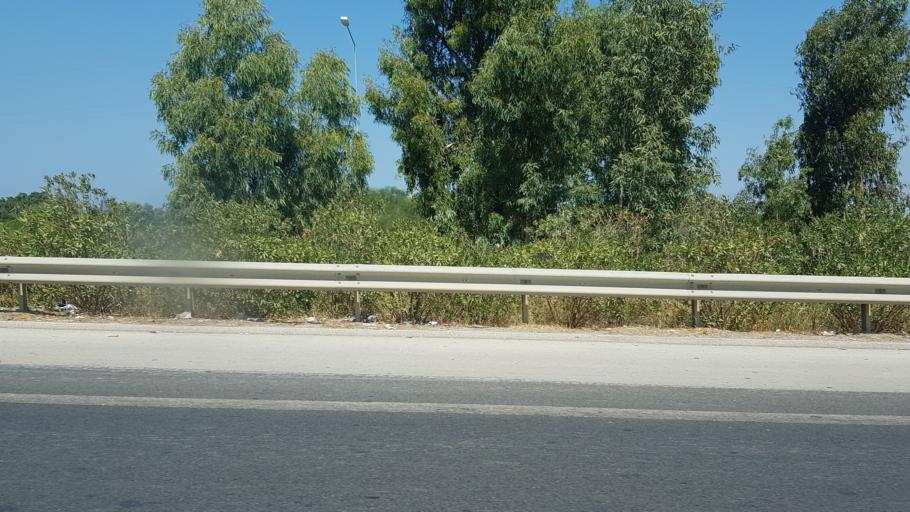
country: TR
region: Izmir
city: Karsiyaka
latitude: 38.3994
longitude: 27.0654
